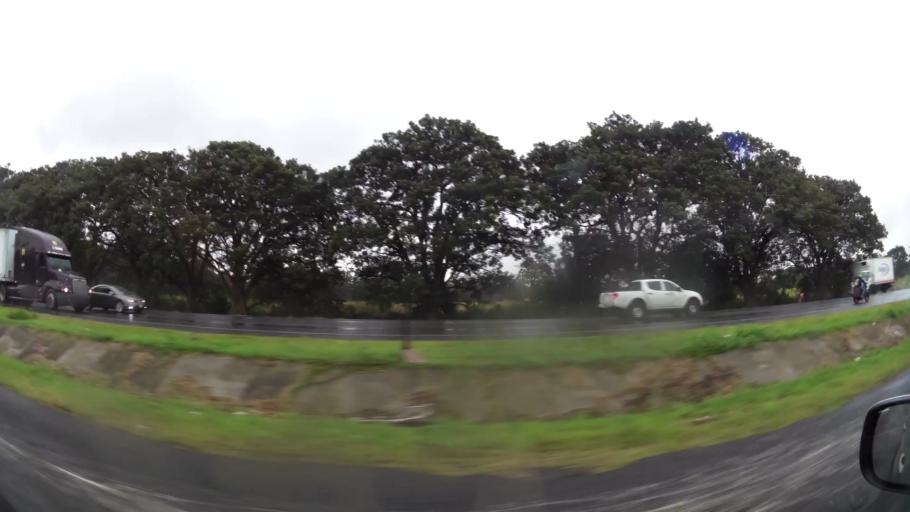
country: CR
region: Alajuela
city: Carrillos
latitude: 9.9947
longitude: -84.2565
